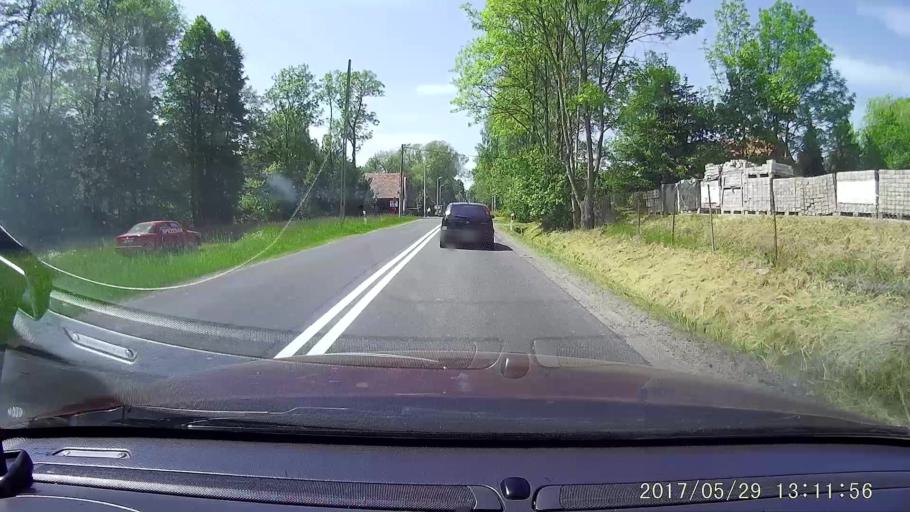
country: PL
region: Lower Silesian Voivodeship
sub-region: Powiat lwowecki
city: Lubomierz
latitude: 50.9663
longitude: 15.5127
